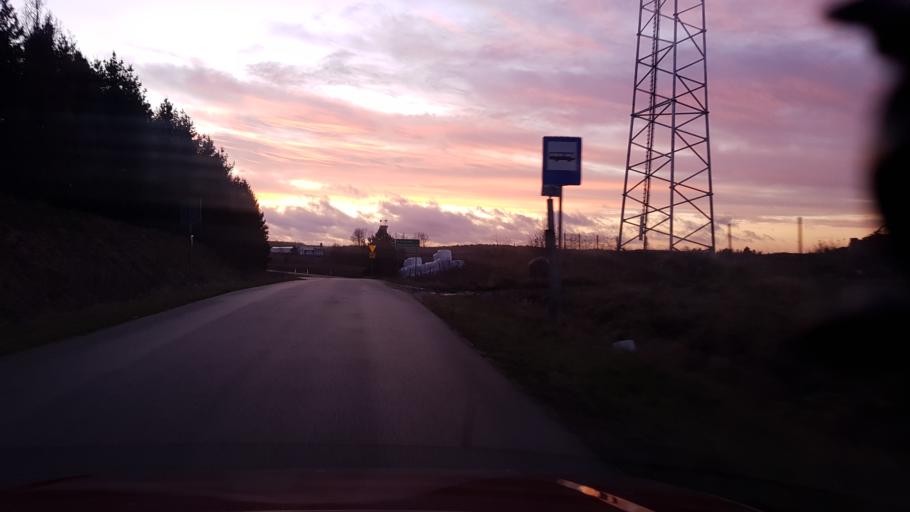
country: PL
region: Pomeranian Voivodeship
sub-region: Powiat bytowski
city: Tuchomie
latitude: 54.1234
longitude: 17.3406
